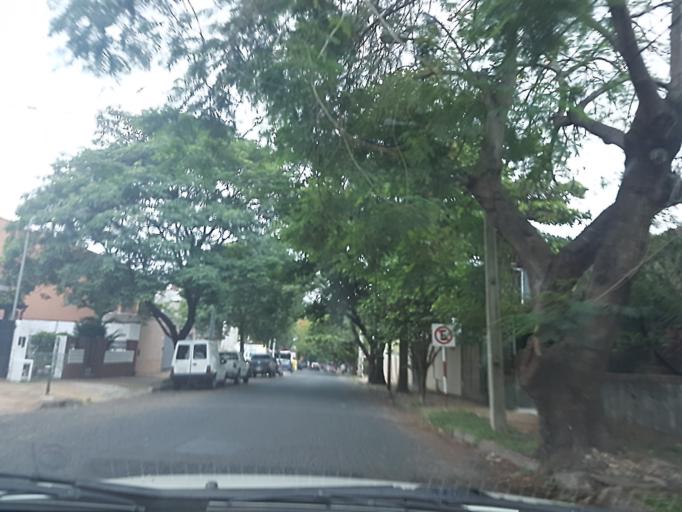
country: PY
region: Asuncion
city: Asuncion
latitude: -25.2862
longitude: -57.6142
